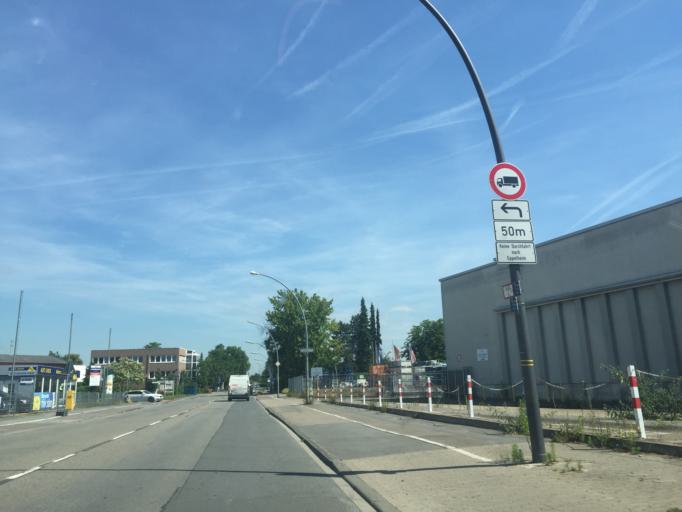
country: DE
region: Baden-Wuerttemberg
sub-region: Karlsruhe Region
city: Eppelheim
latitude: 49.4074
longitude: 8.6406
